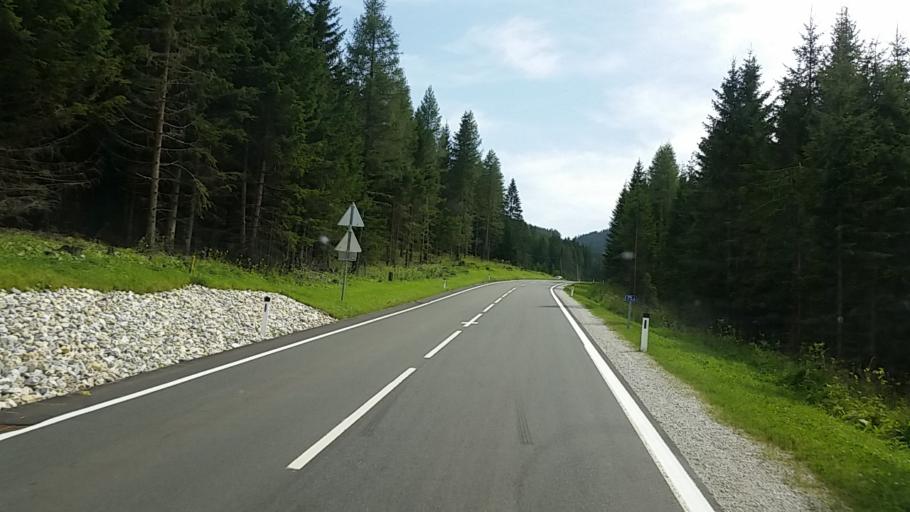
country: AT
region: Salzburg
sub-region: Politischer Bezirk Tamsweg
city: Sankt Michael im Lungau
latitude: 47.0751
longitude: 13.6178
